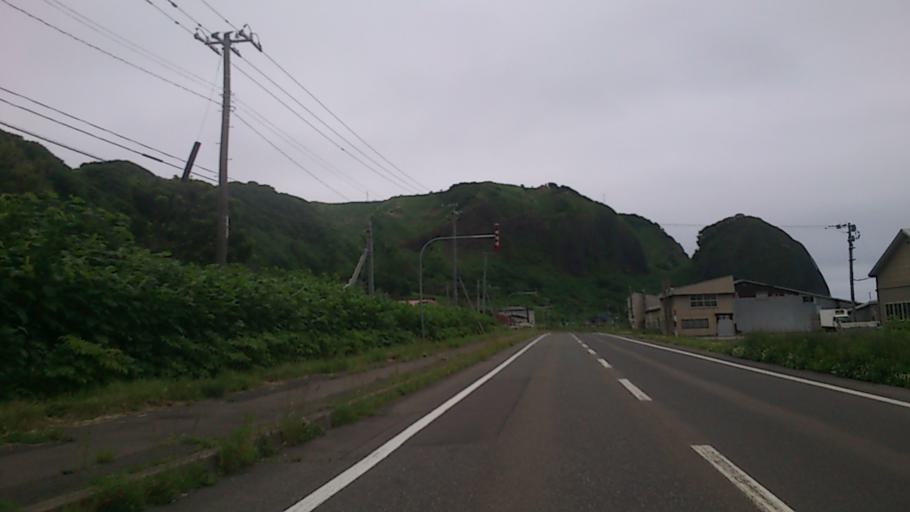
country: JP
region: Hokkaido
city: Iwanai
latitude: 42.4635
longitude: 139.8537
